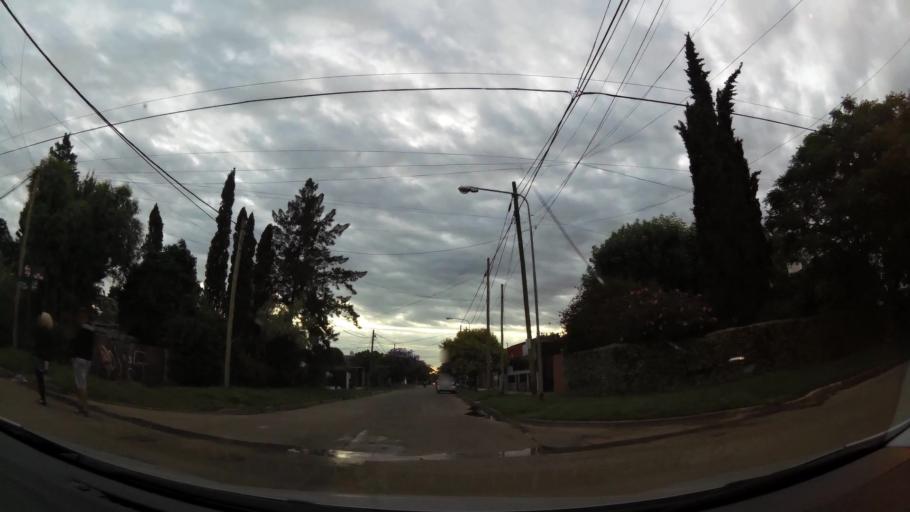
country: AR
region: Buenos Aires
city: Santa Catalina - Dique Lujan
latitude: -34.4144
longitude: -58.6870
